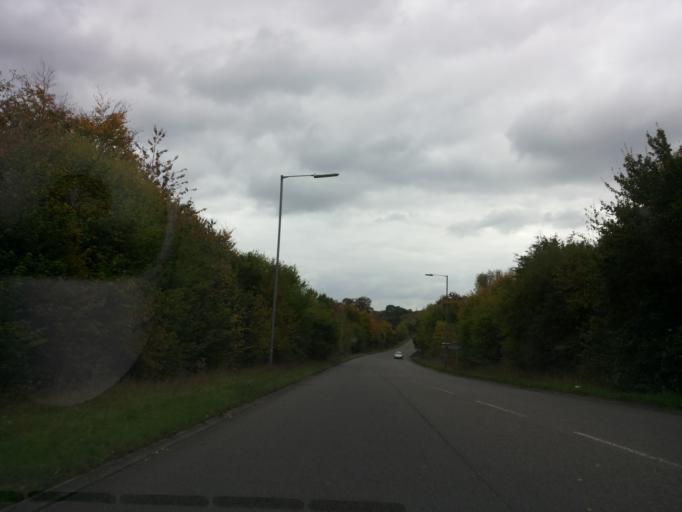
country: GB
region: England
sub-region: Buckinghamshire
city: Amersham
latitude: 51.6731
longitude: -0.6318
